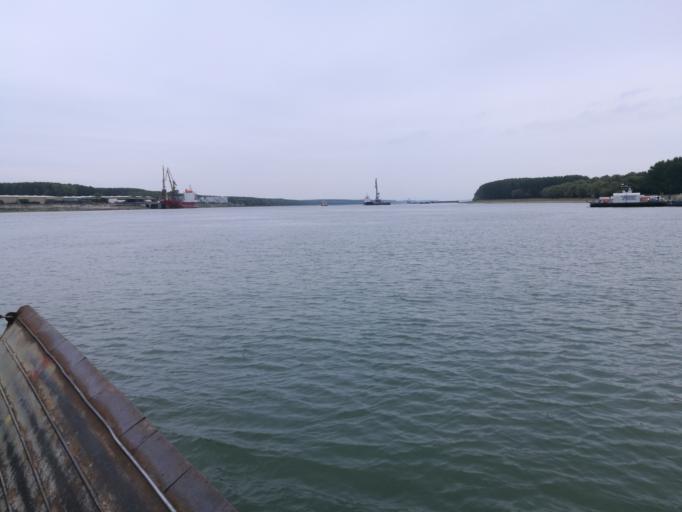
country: RO
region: Braila
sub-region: Municipiul Braila
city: Braila
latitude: 45.2870
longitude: 27.9955
